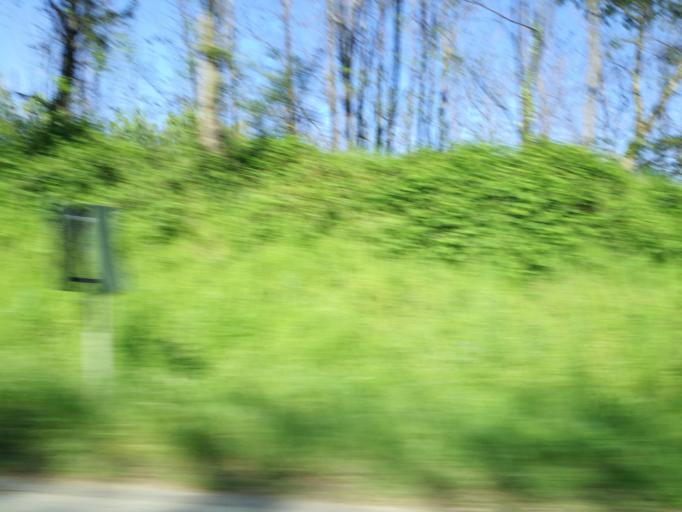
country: IT
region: Lombardy
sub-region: Provincia di Bergamo
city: Carvico
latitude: 45.7007
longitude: 9.4754
